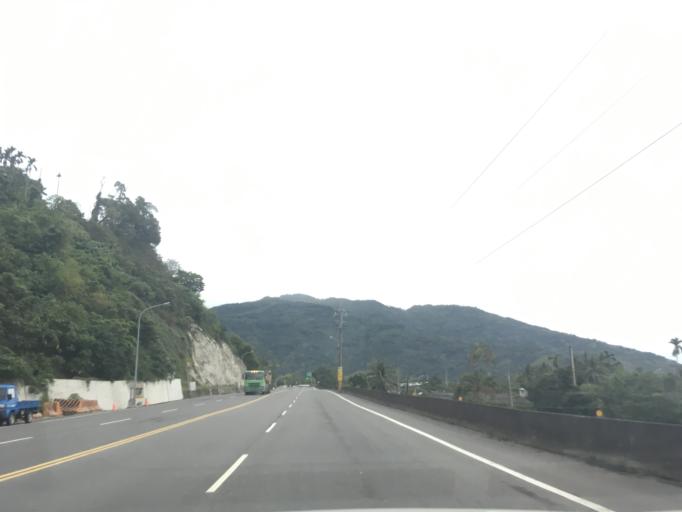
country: TW
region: Taiwan
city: Taitung City
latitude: 22.7530
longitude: 121.0538
